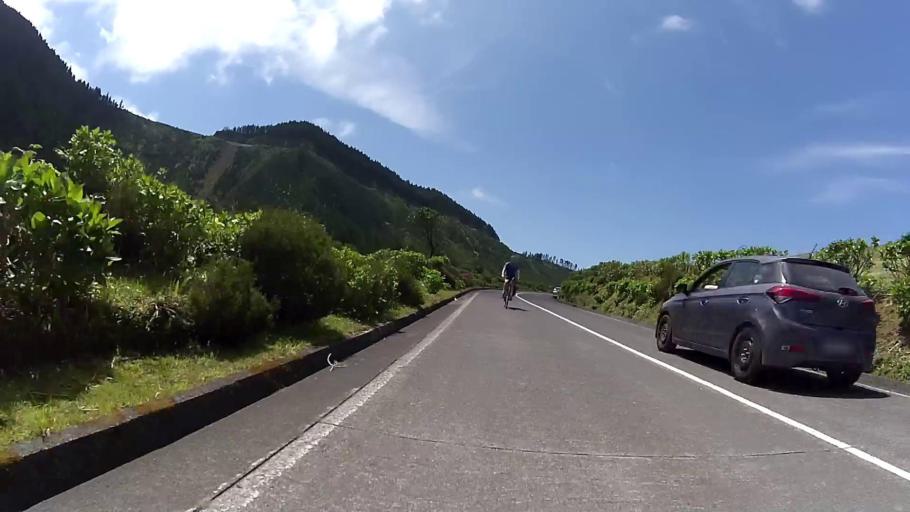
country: PT
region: Azores
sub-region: Ponta Delgada
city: Arrifes
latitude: 37.8431
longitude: -25.7727
